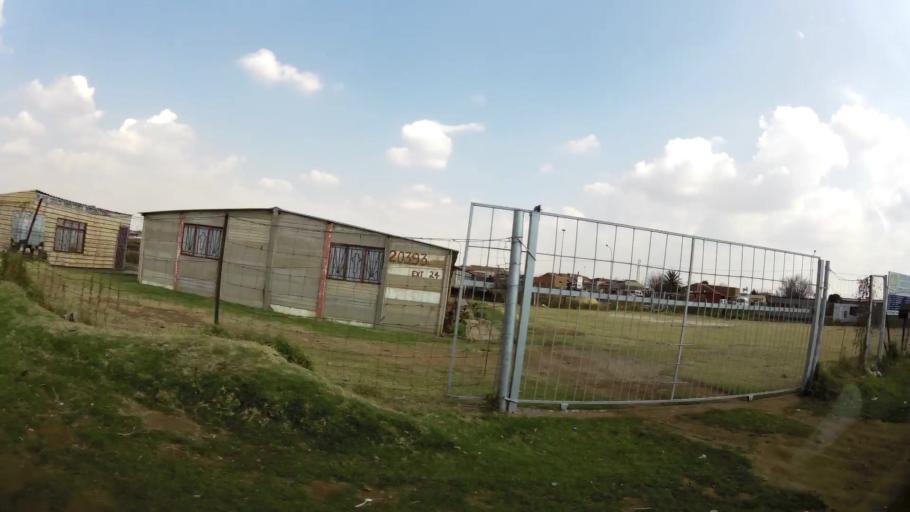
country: ZA
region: Gauteng
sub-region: Ekurhuleni Metropolitan Municipality
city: Springs
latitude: -26.1268
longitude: 28.4773
